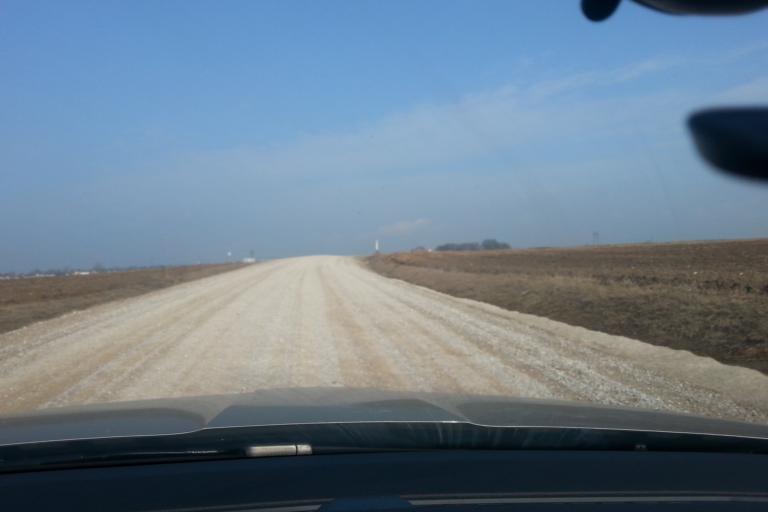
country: LT
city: Trakai
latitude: 54.5975
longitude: 24.9783
